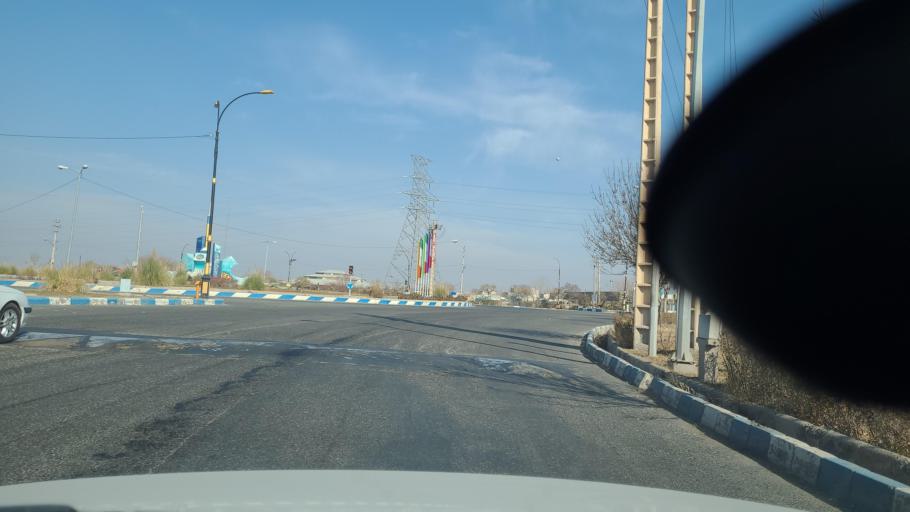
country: IR
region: Razavi Khorasan
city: Fariman
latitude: 35.7057
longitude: 59.8361
